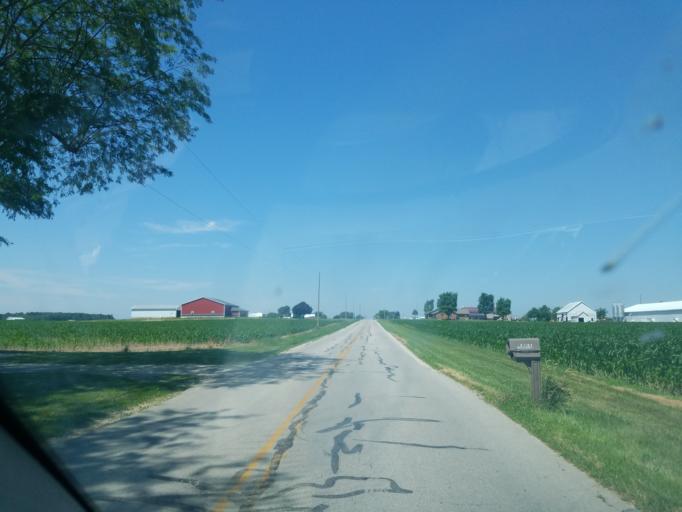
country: US
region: Ohio
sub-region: Mercer County
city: Saint Henry
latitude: 40.4506
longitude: -84.6674
